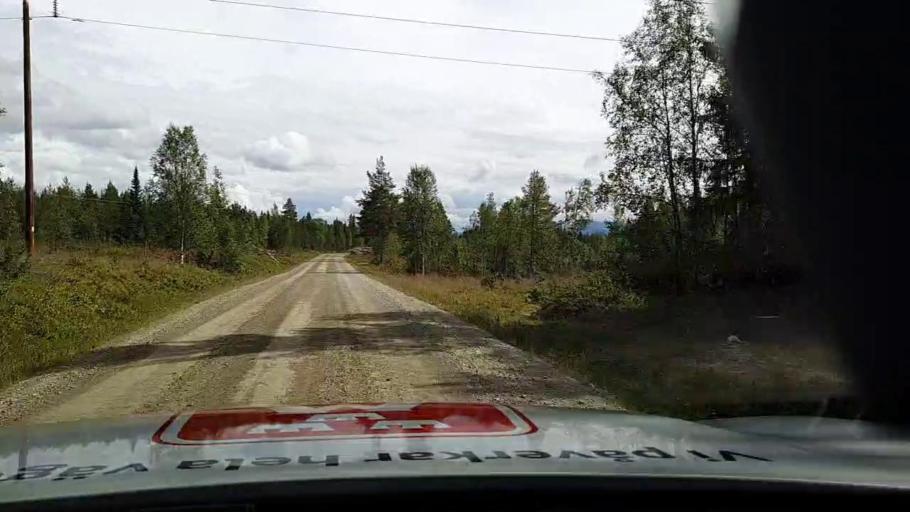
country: SE
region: Jaemtland
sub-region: Are Kommun
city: Jarpen
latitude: 62.5285
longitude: 13.4855
